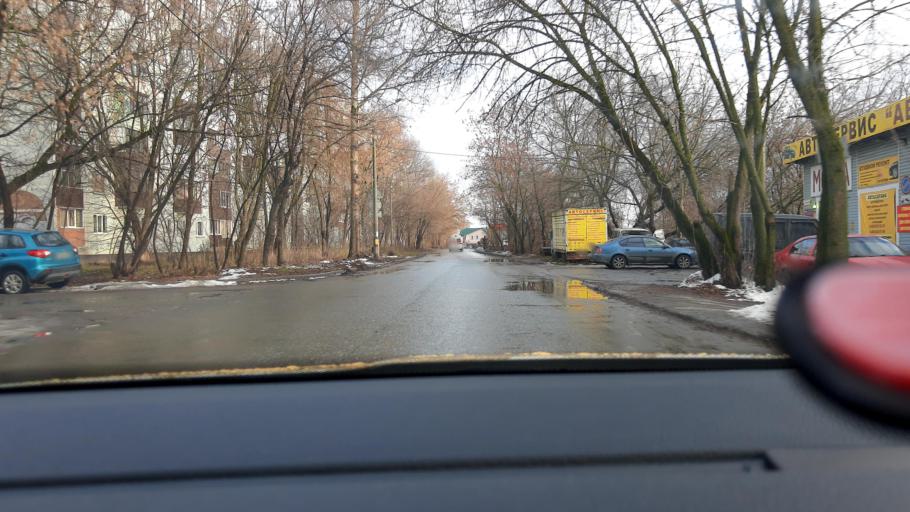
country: RU
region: Moskovskaya
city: Pushkino
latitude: 55.9923
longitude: 37.8629
